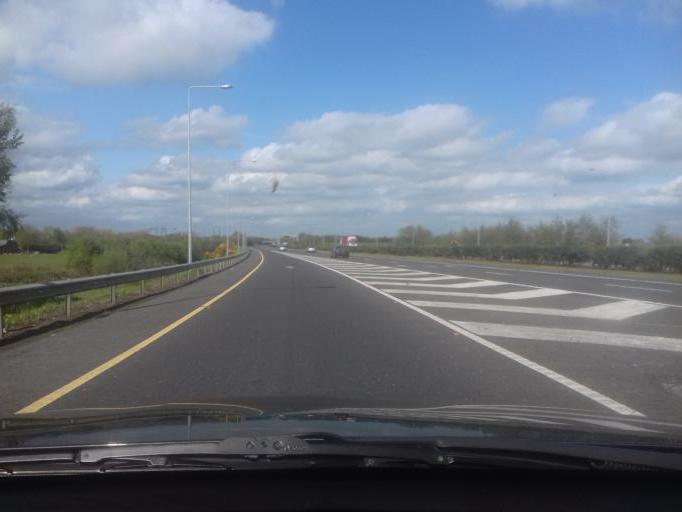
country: IE
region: Leinster
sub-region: Laois
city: Portlaoise
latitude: 53.0531
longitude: -7.2365
